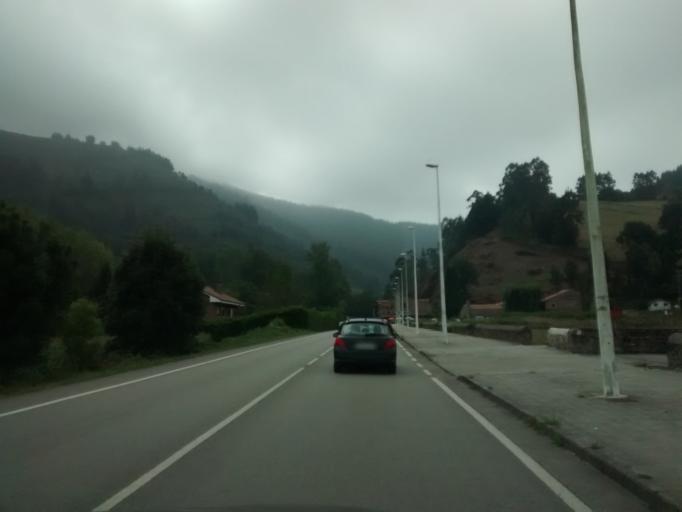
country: ES
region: Cantabria
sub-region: Provincia de Cantabria
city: Cabezon de la Sal
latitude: 43.2873
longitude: -4.2360
